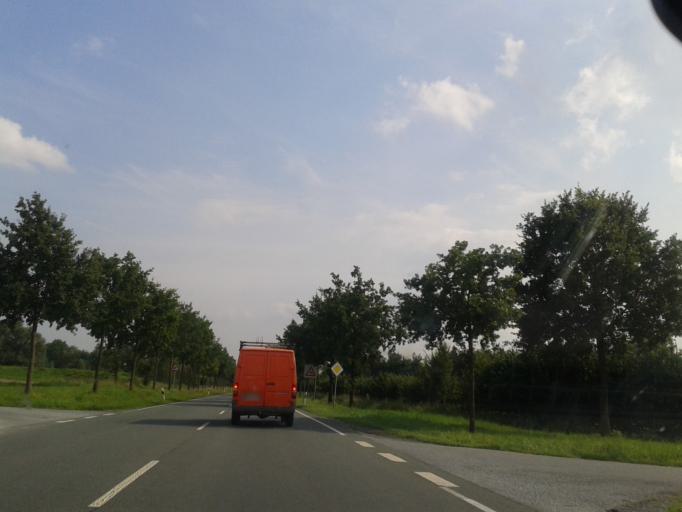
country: DE
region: North Rhine-Westphalia
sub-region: Regierungsbezirk Detmold
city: Paderborn
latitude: 51.7453
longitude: 8.7809
